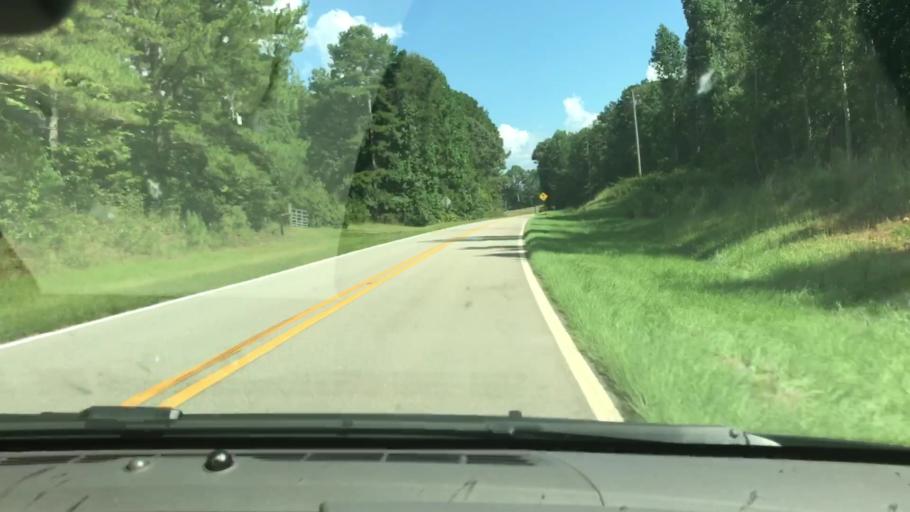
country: US
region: Georgia
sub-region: Troup County
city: La Grange
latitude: 33.1451
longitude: -85.1113
